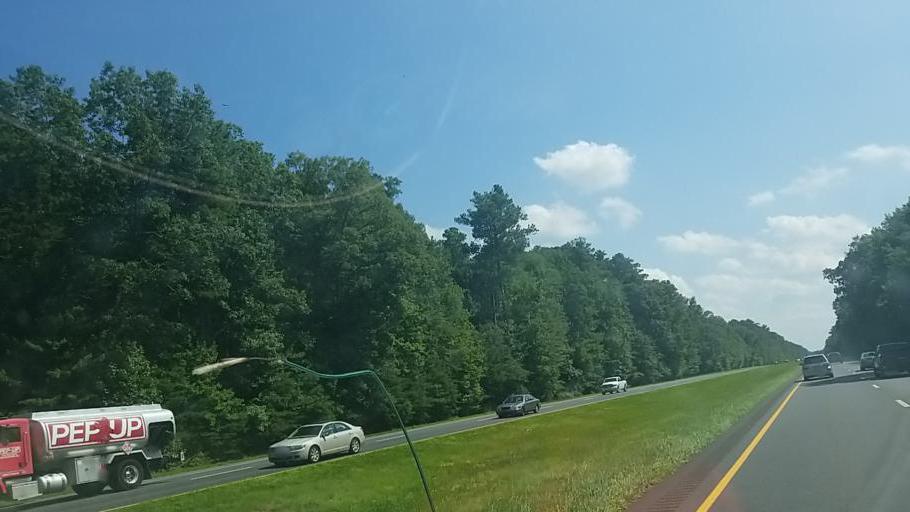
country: US
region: Delaware
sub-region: Sussex County
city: Georgetown
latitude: 38.7857
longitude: -75.4387
